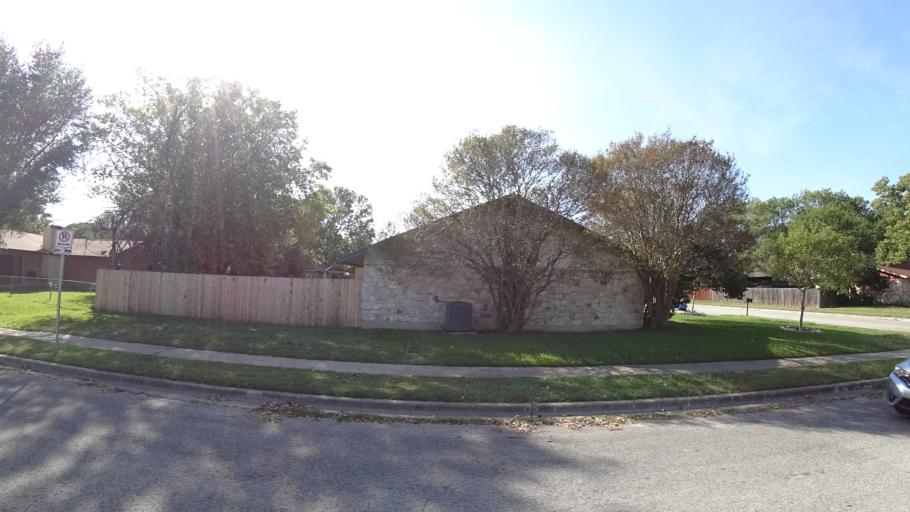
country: US
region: Texas
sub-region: Williamson County
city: Anderson Mill
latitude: 30.4559
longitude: -97.7996
